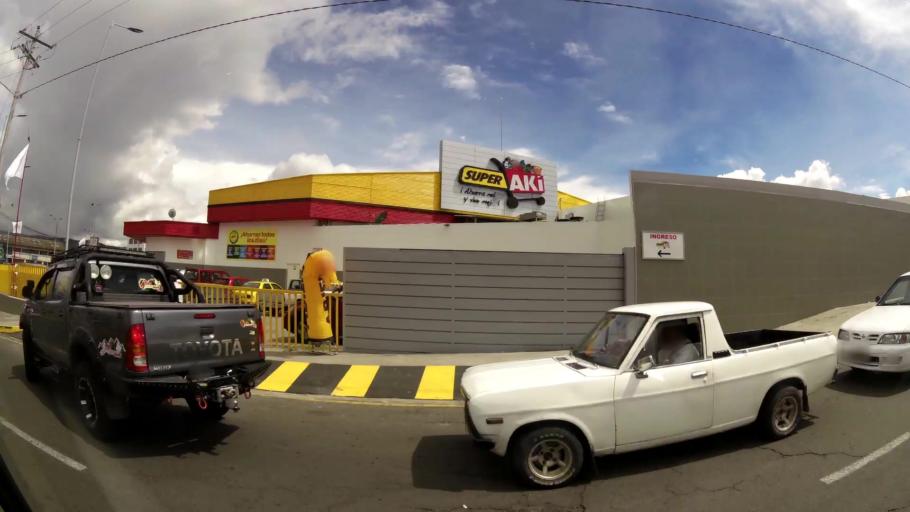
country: EC
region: Tungurahua
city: Ambato
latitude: -1.2680
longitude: -78.6125
